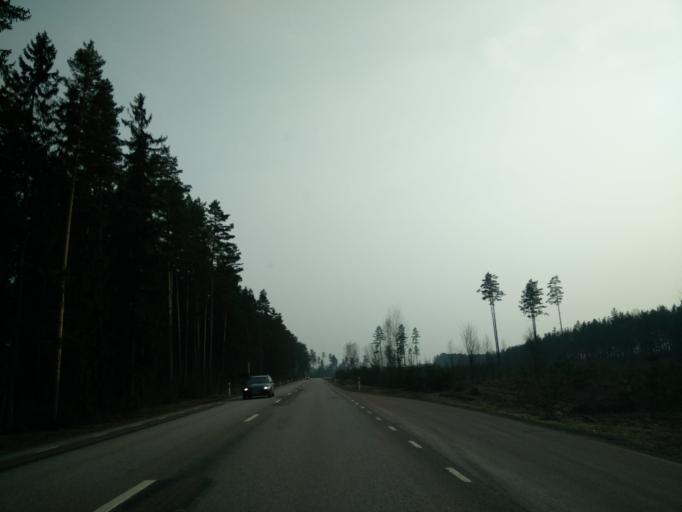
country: SE
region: Vaermland
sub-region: Forshaga Kommun
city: Forshaga
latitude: 59.5034
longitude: 13.4349
